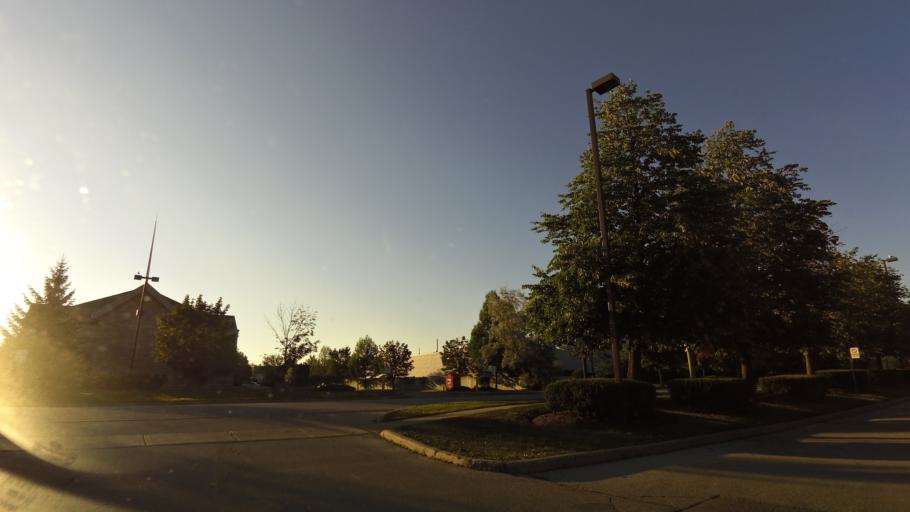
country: CA
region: Ontario
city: Brampton
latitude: 43.5962
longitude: -79.7580
